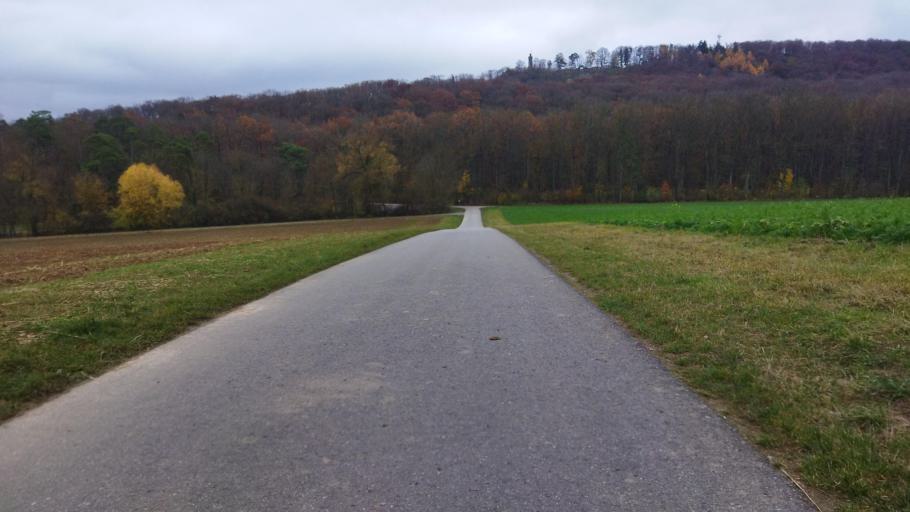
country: DE
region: Baden-Wuerttemberg
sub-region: Regierungsbezirk Stuttgart
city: Leingarten
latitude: 49.1353
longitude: 9.1061
